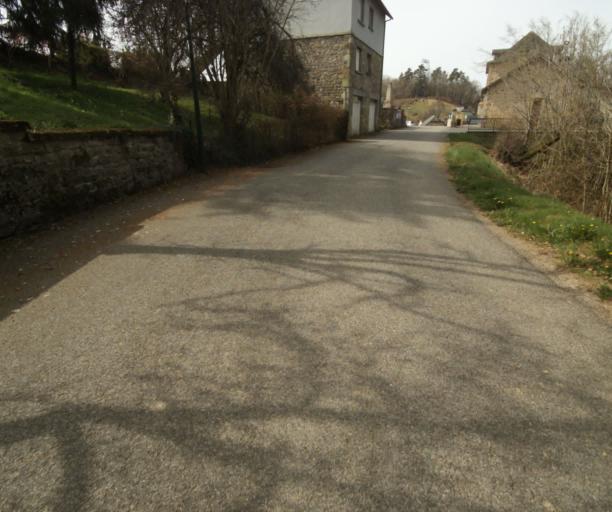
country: FR
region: Limousin
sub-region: Departement de la Correze
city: Naves
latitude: 45.3453
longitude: 1.8147
